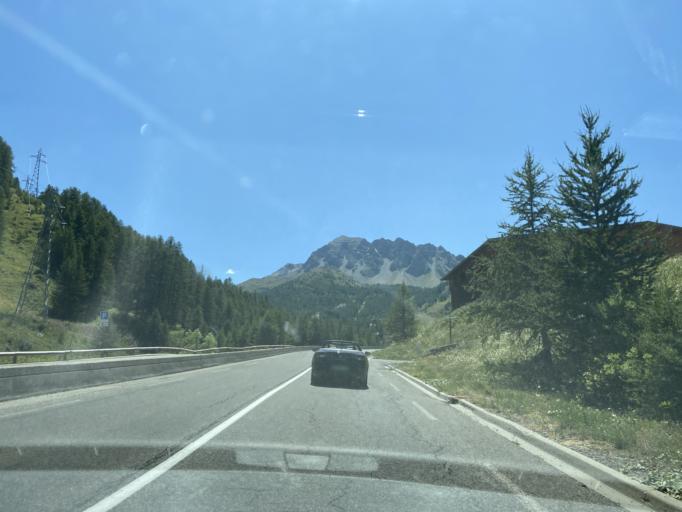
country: FR
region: Provence-Alpes-Cote d'Azur
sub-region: Departement des Hautes-Alpes
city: Guillestre
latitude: 44.5801
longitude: 6.6844
